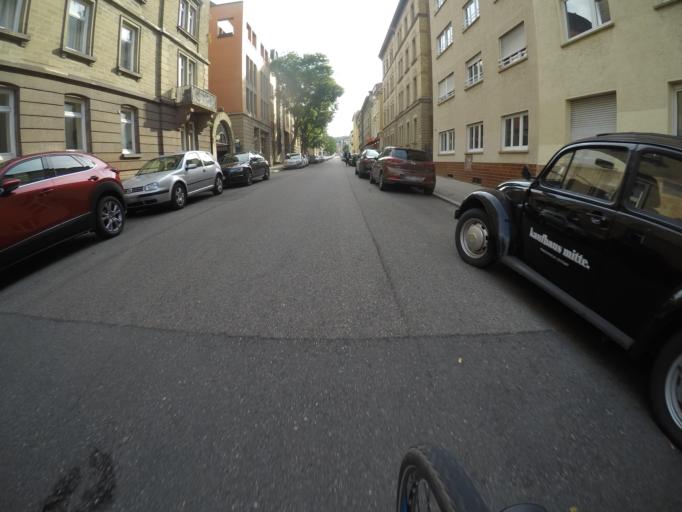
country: DE
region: Baden-Wuerttemberg
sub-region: Regierungsbezirk Stuttgart
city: Stuttgart
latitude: 48.7746
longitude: 9.1634
